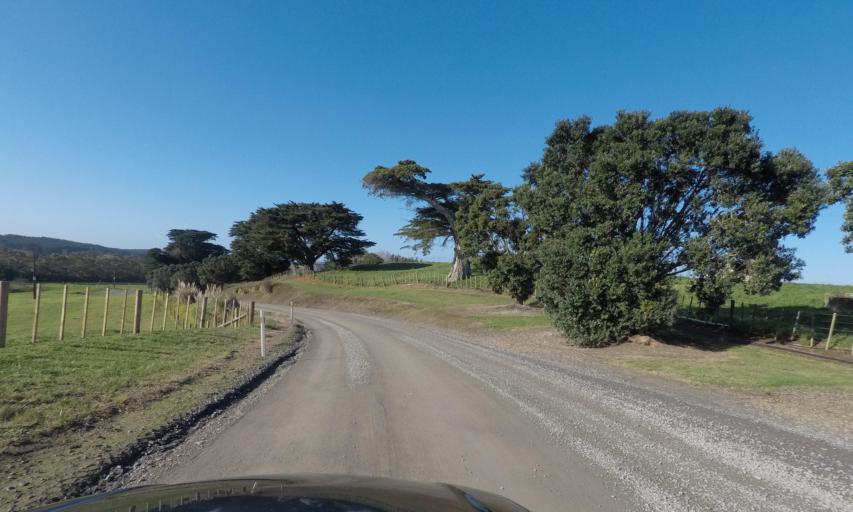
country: NZ
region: Auckland
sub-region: Auckland
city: Wellsford
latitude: -36.1444
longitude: 174.5970
